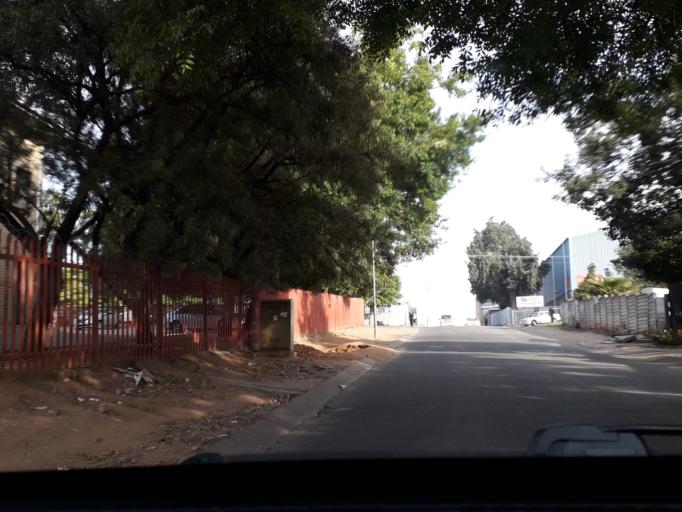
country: ZA
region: Gauteng
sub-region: City of Johannesburg Metropolitan Municipality
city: Modderfontein
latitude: -26.1241
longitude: 28.0872
